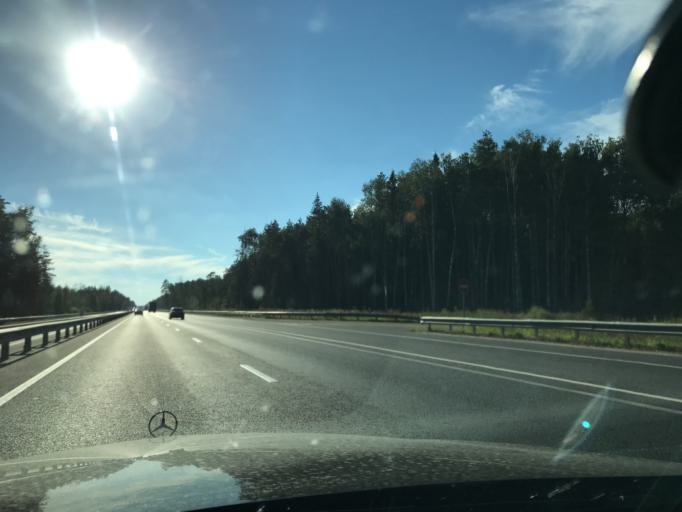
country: RU
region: Vladimir
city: Nikologory
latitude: 56.2352
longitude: 41.8845
